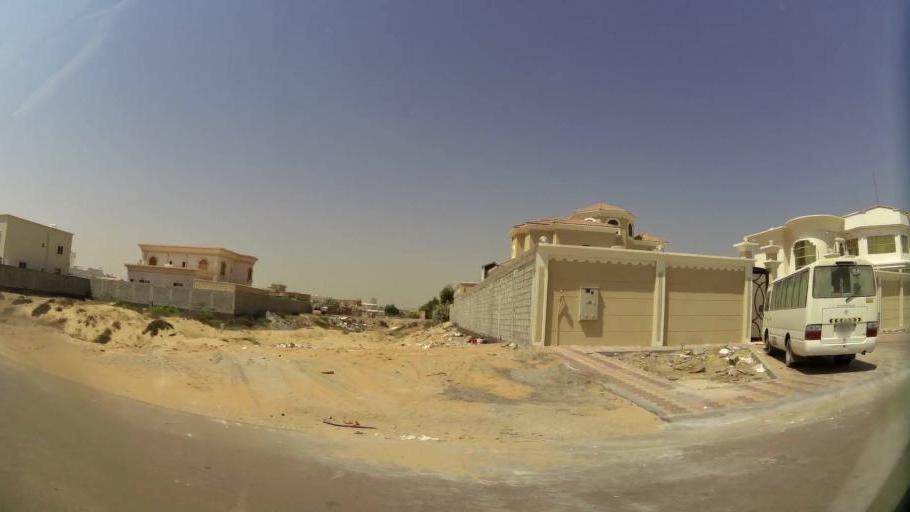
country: AE
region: Ajman
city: Ajman
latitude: 25.4253
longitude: 55.5227
